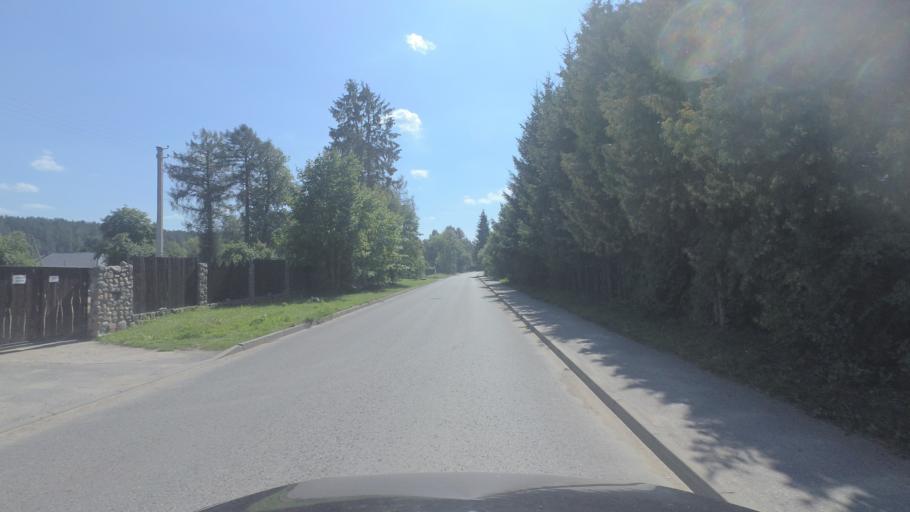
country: LT
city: Nemencine
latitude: 54.8382
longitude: 25.3707
